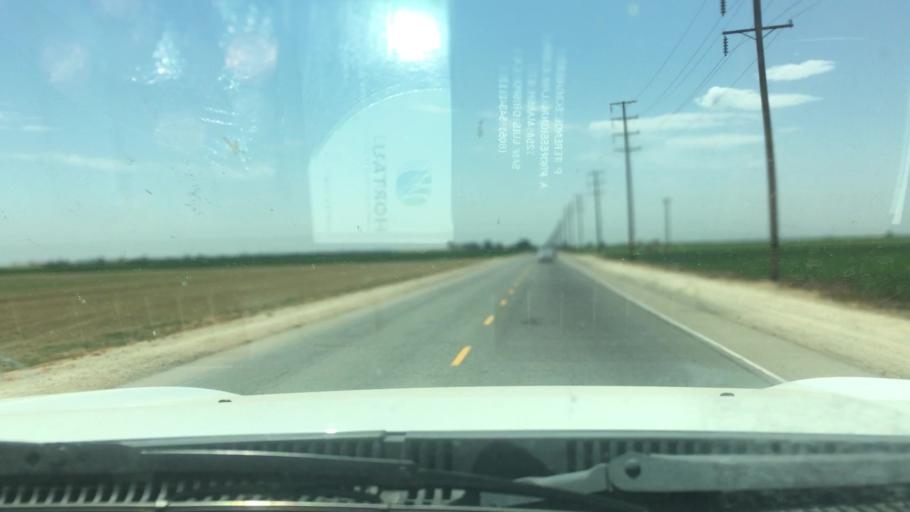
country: US
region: California
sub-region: Tulare County
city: Tipton
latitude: 36.0657
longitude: -119.2752
